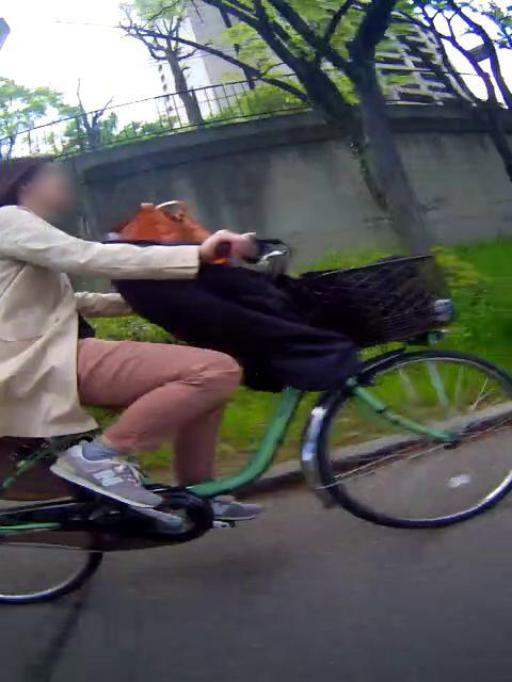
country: JP
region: Osaka
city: Osaka-shi
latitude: 34.6977
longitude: 135.5234
